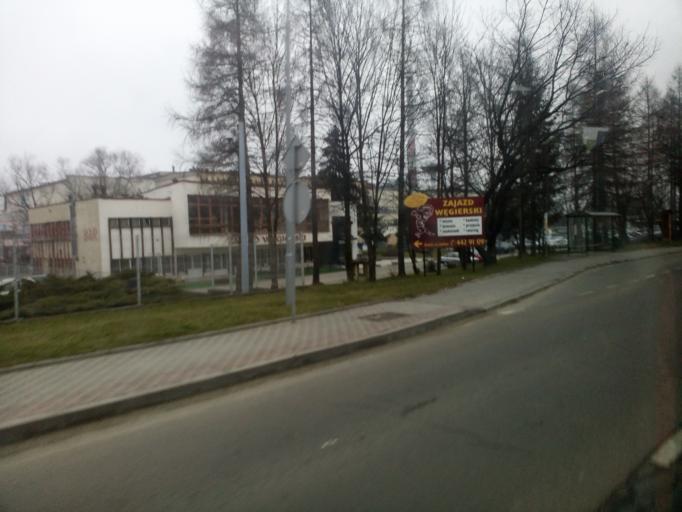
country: PL
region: Lesser Poland Voivodeship
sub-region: Powiat nowosadecki
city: Nowy Sacz
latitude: 49.5917
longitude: 20.6782
